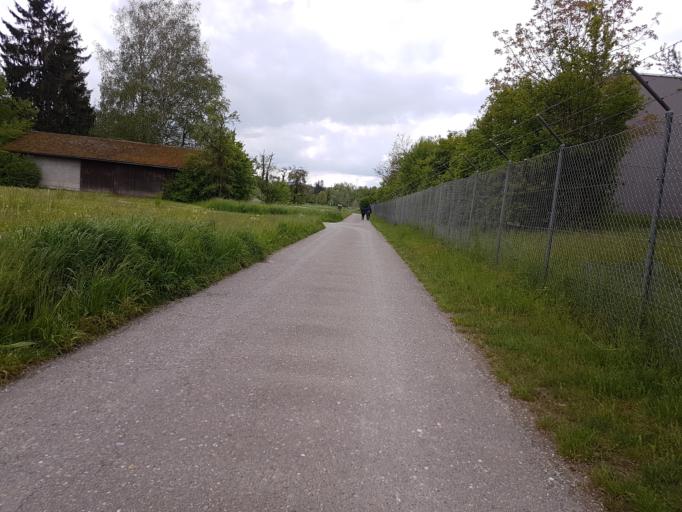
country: CH
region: Aargau
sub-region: Bezirk Brugg
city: Lauffohr (Brugg)
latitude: 47.4920
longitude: 8.2310
